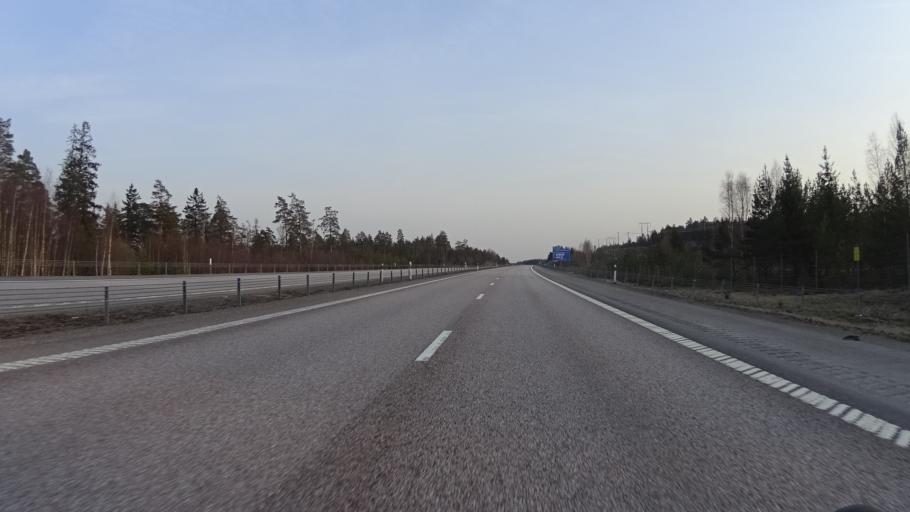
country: SE
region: Soedermanland
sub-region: Strangnas Kommun
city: Strangnas
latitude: 59.3469
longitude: 17.0096
